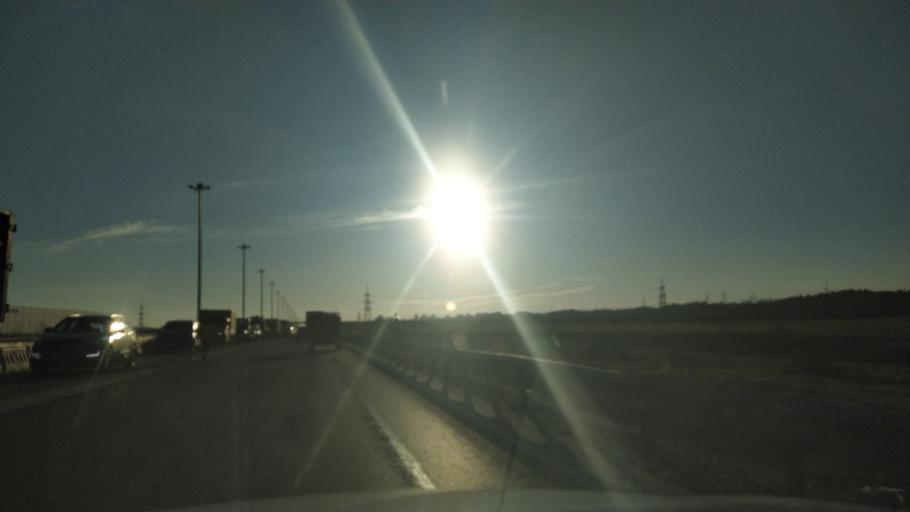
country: RU
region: Leningrad
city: Parnas
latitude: 60.0948
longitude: 30.3470
